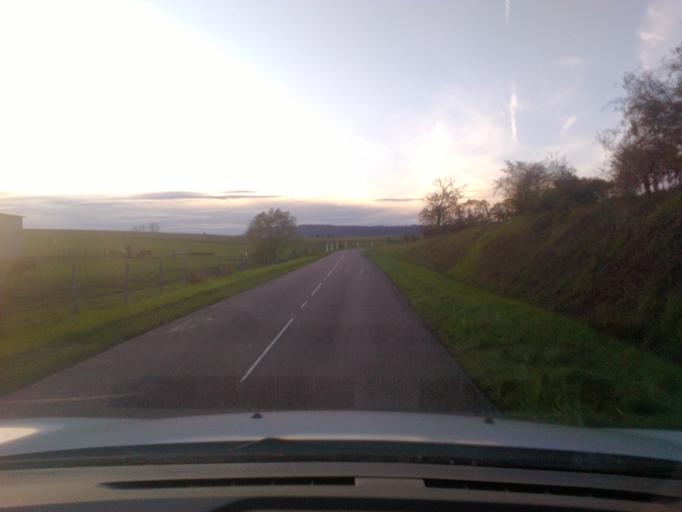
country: FR
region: Lorraine
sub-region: Departement des Vosges
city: Mirecourt
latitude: 48.4031
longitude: 6.1539
